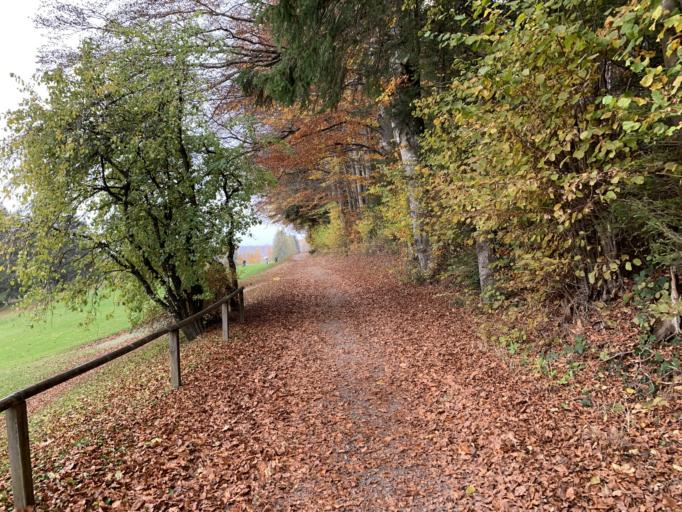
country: CH
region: Zurich
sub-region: Bezirk Hinwil
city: Baretswil
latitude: 47.3574
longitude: 8.8496
